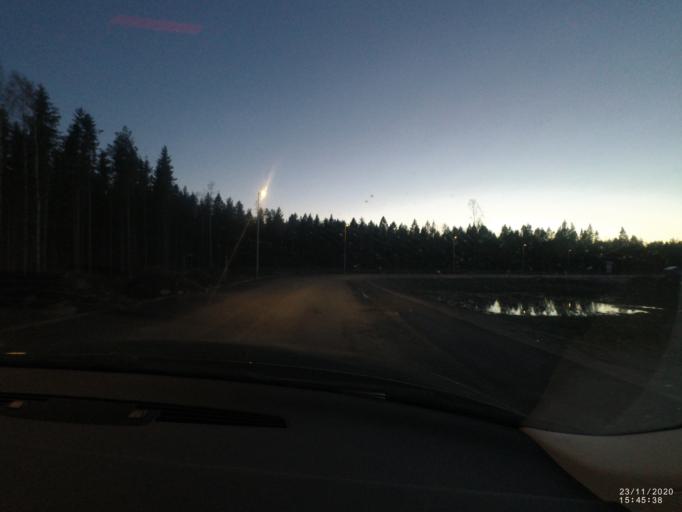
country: SE
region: Soedermanland
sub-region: Oxelosunds Kommun
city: Bara
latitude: 58.7255
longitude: 17.0681
